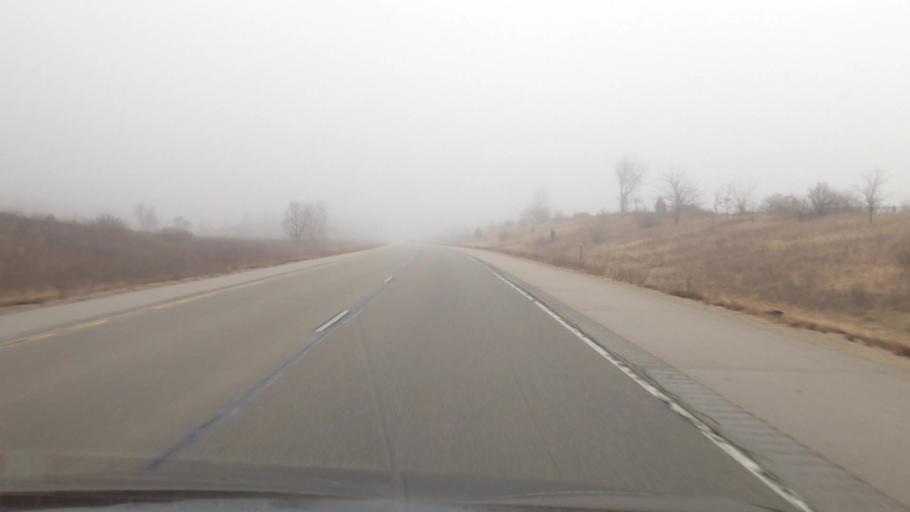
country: US
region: Wisconsin
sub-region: Walworth County
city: East Troy
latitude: 42.7561
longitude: -88.4349
